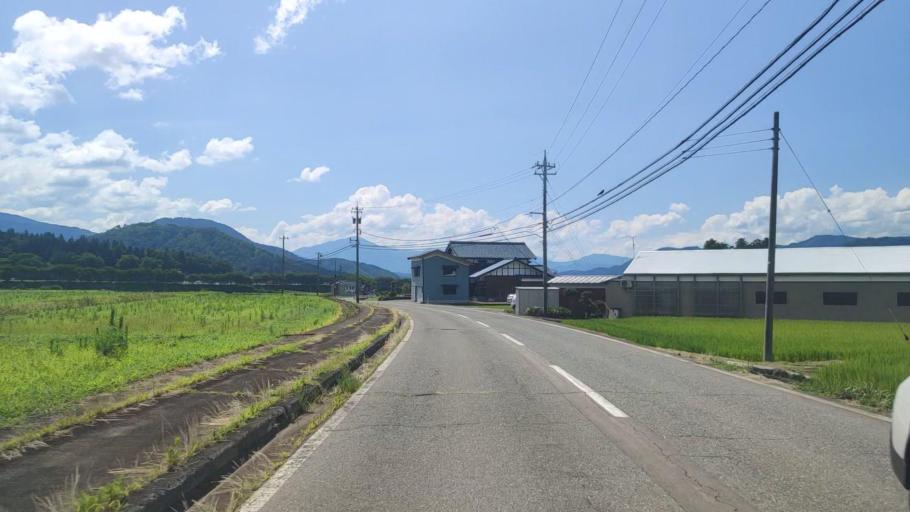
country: JP
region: Fukui
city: Katsuyama
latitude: 36.0877
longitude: 136.4931
